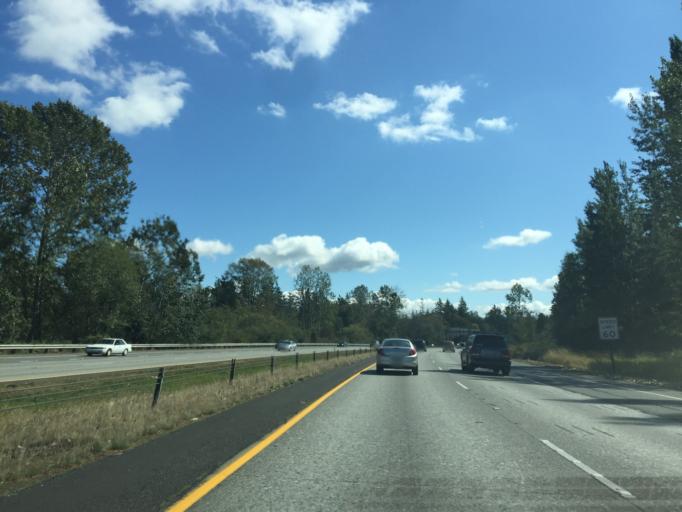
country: US
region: Washington
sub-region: Whatcom County
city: Bellingham
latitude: 48.7816
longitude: -122.4784
